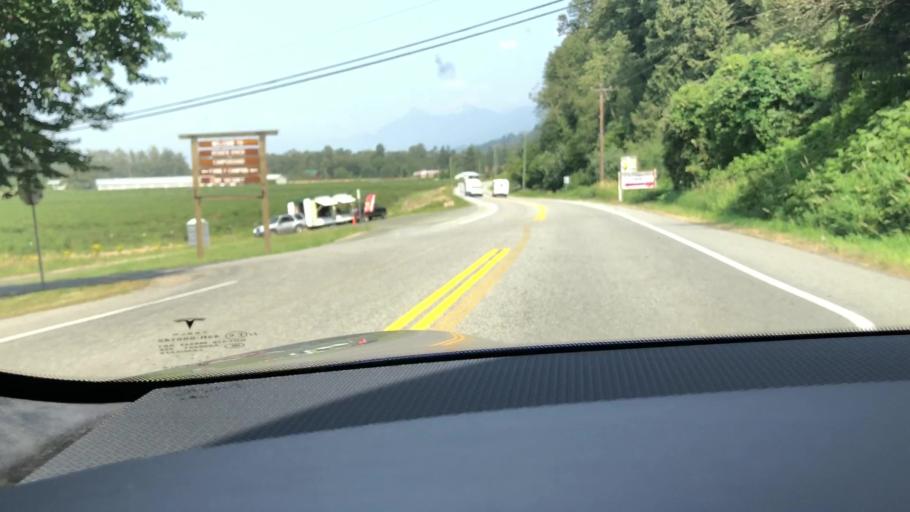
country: CA
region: British Columbia
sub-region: Fraser Valley Regional District
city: Chilliwack
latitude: 49.0896
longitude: -122.0070
